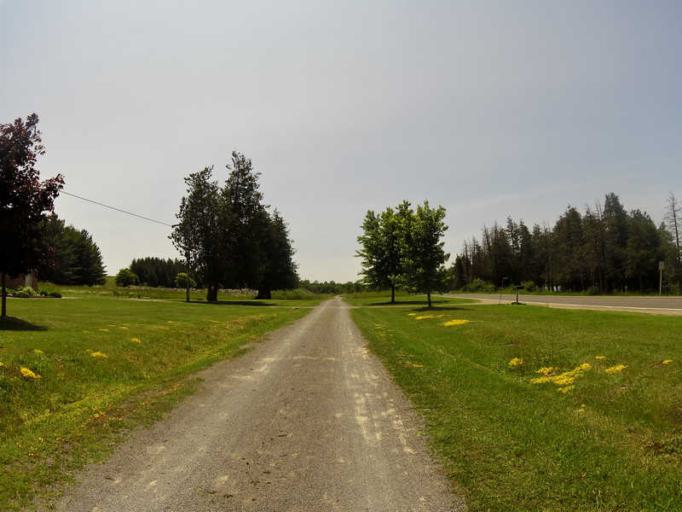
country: CA
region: Ontario
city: Peterborough
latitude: 44.4064
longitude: -78.2615
